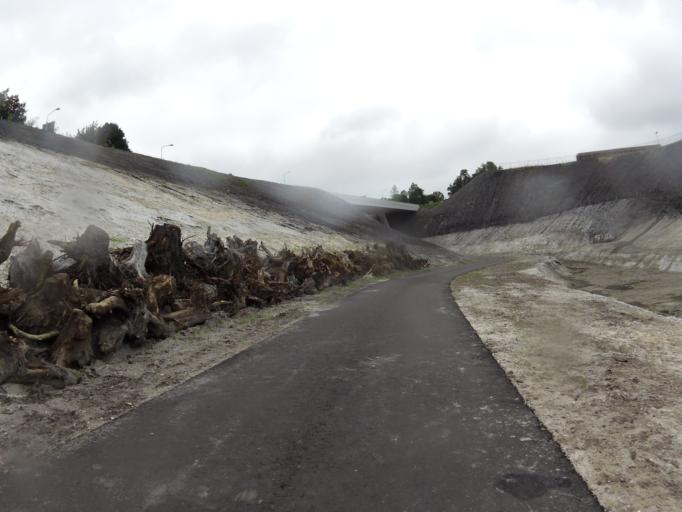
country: NL
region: Limburg
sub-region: Gemeente Brunssum
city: Brunssum
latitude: 50.9409
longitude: 5.9877
